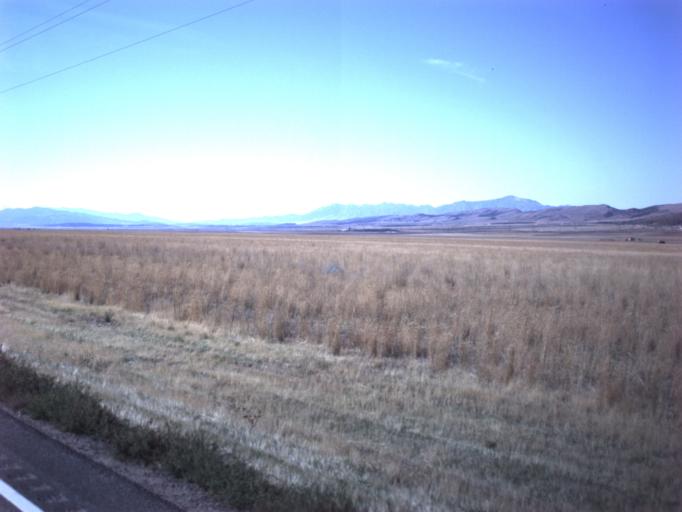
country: US
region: Utah
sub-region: Juab County
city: Nephi
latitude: 39.6234
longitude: -111.8618
